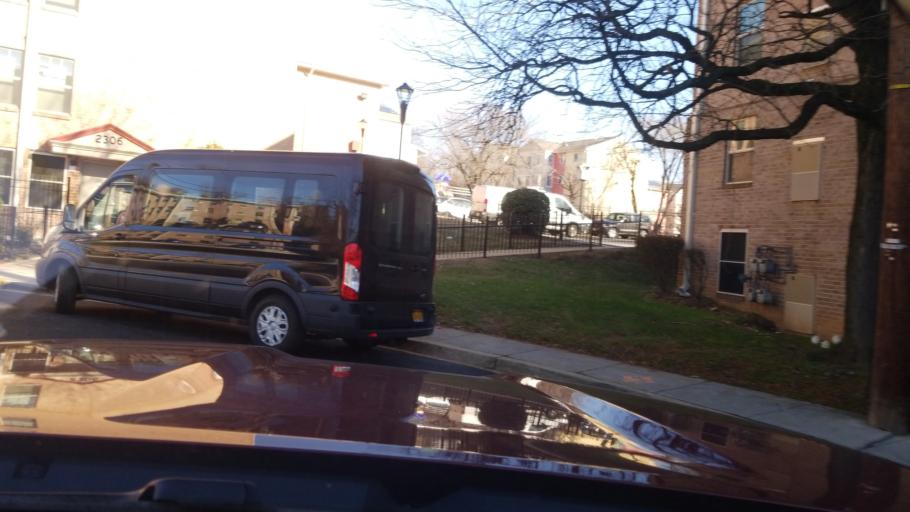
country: US
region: Maryland
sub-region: Prince George's County
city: Hillcrest Heights
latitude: 38.8548
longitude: -76.9726
